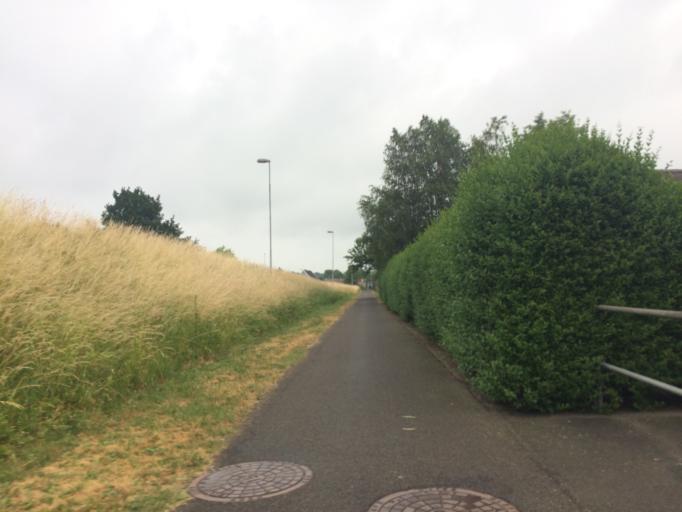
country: DK
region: Capital Region
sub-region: Bornholm Kommune
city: Ronne
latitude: 55.1007
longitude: 14.7194
